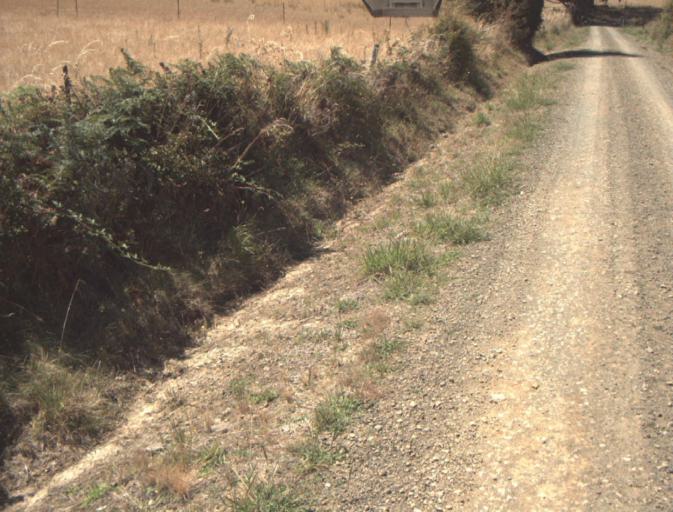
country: AU
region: Tasmania
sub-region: Launceston
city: Mayfield
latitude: -41.2666
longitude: 147.1417
